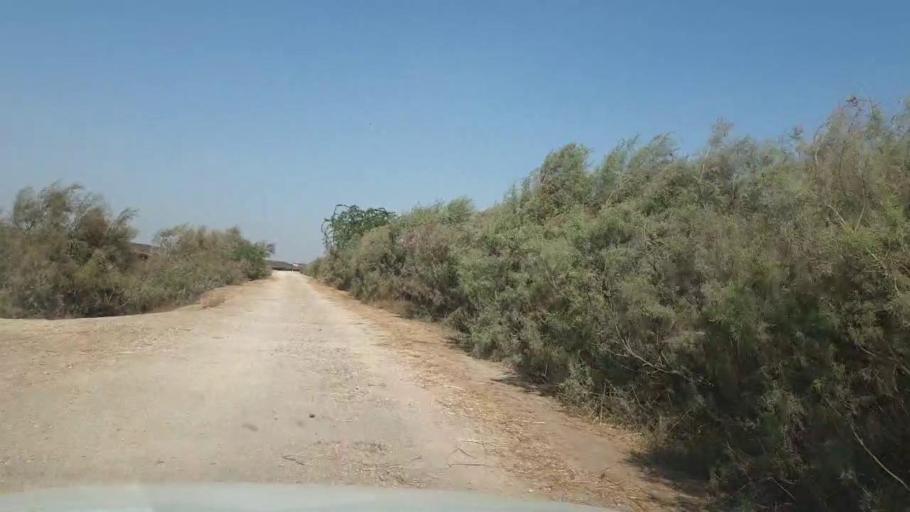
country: PK
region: Sindh
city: Chuhar Jamali
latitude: 24.3770
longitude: 67.8021
